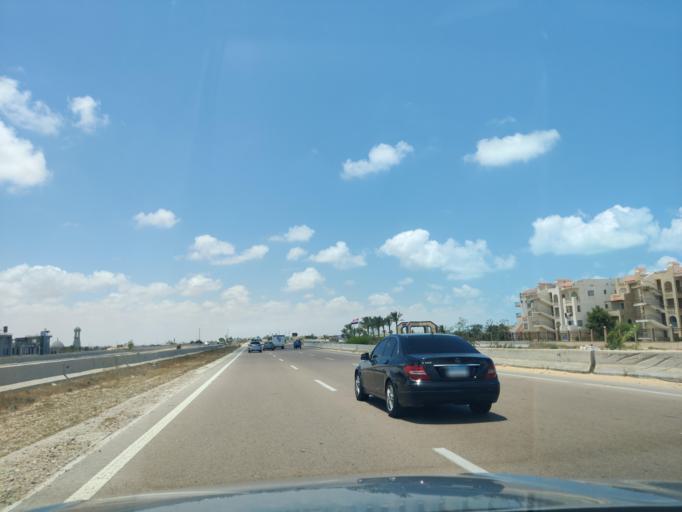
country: EG
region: Muhafazat Matruh
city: Al `Alamayn
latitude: 30.8125
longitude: 29.0873
